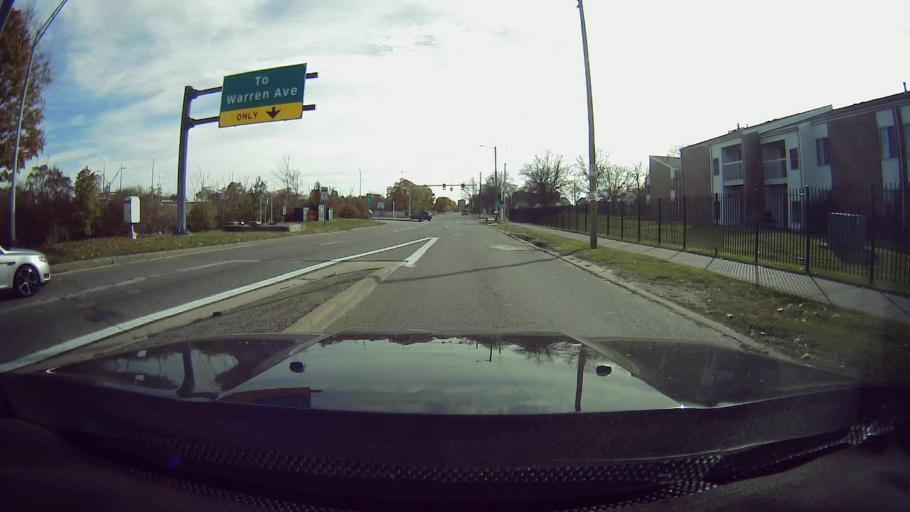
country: US
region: Michigan
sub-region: Wayne County
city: Detroit
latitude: 42.3521
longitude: -83.0730
